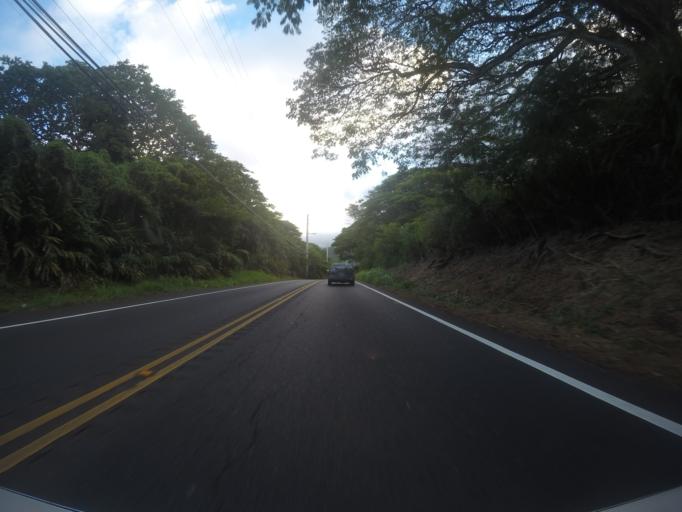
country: US
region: Hawaii
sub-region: Honolulu County
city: Ka'a'awa
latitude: 21.5142
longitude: -157.8458
